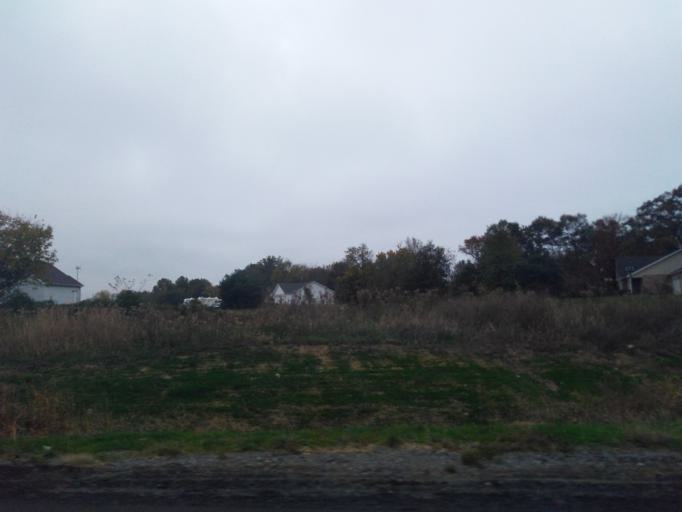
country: US
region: Illinois
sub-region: Madison County
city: Highland
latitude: 38.7868
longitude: -89.6689
